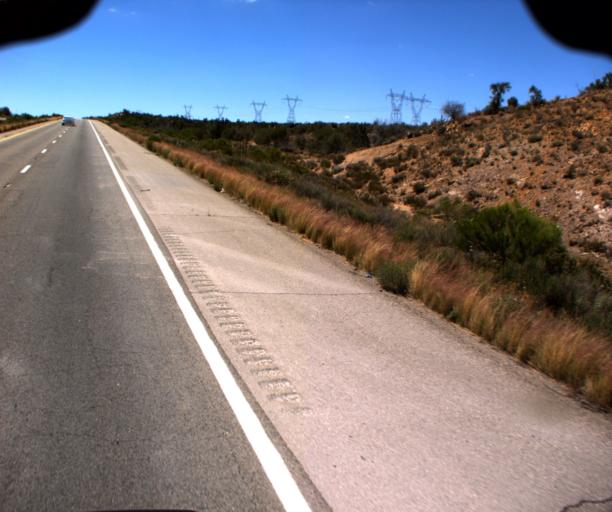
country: US
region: Arizona
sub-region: Yavapai County
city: Bagdad
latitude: 34.4692
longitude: -113.3130
